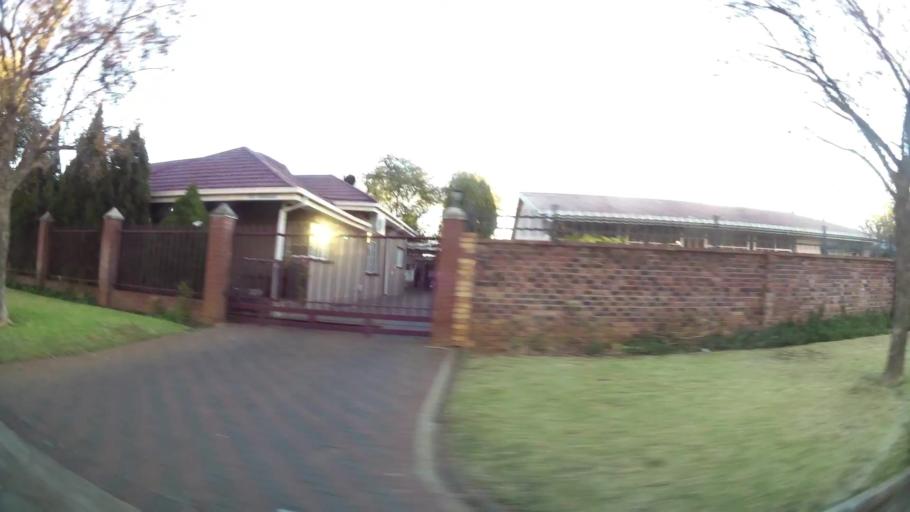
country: ZA
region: North-West
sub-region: Dr Kenneth Kaunda District Municipality
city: Potchefstroom
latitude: -26.7219
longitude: 27.0924
